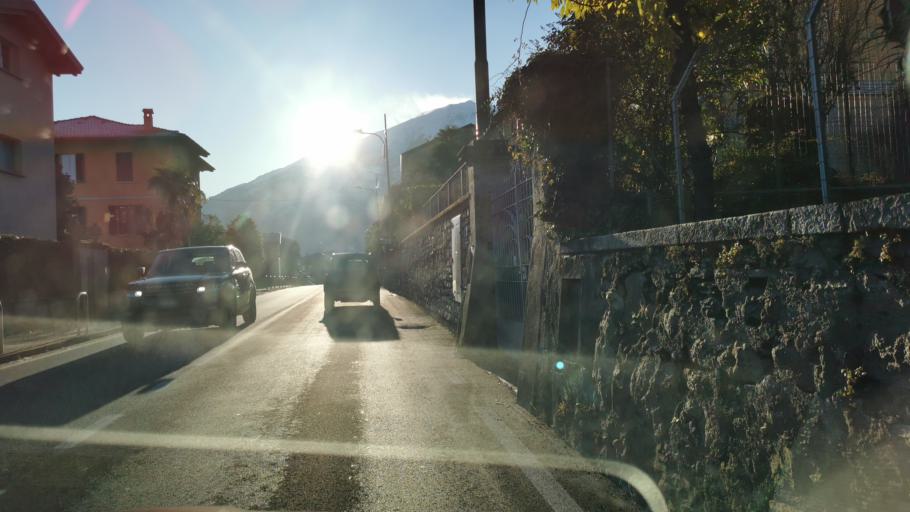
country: IT
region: Lombardy
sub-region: Provincia di Como
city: Gravedona-San Gregorio
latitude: 46.1456
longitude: 9.3014
